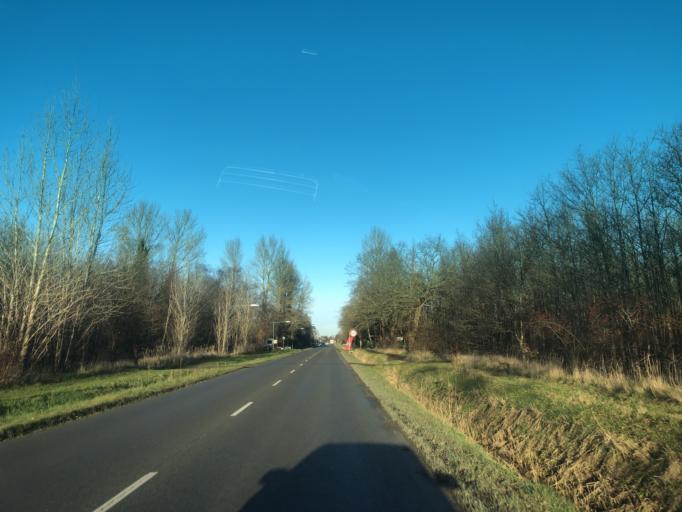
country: DK
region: Capital Region
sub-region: Tarnby Kommune
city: Tarnby
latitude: 55.5835
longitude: 12.5785
